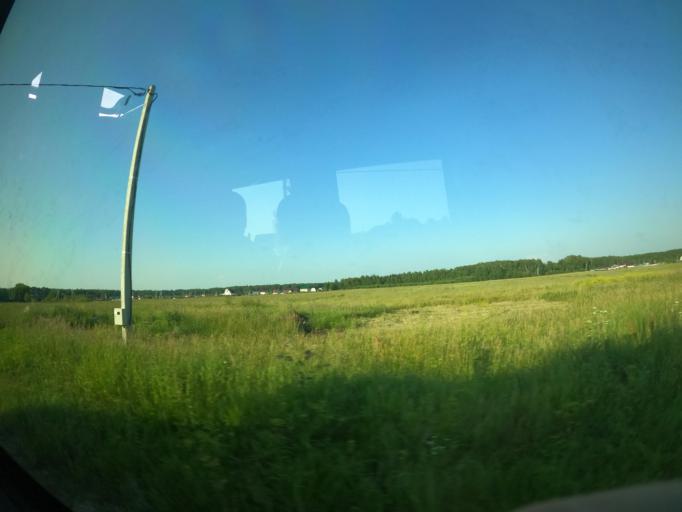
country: RU
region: Moskovskaya
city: Obolensk
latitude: 54.9385
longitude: 37.2448
